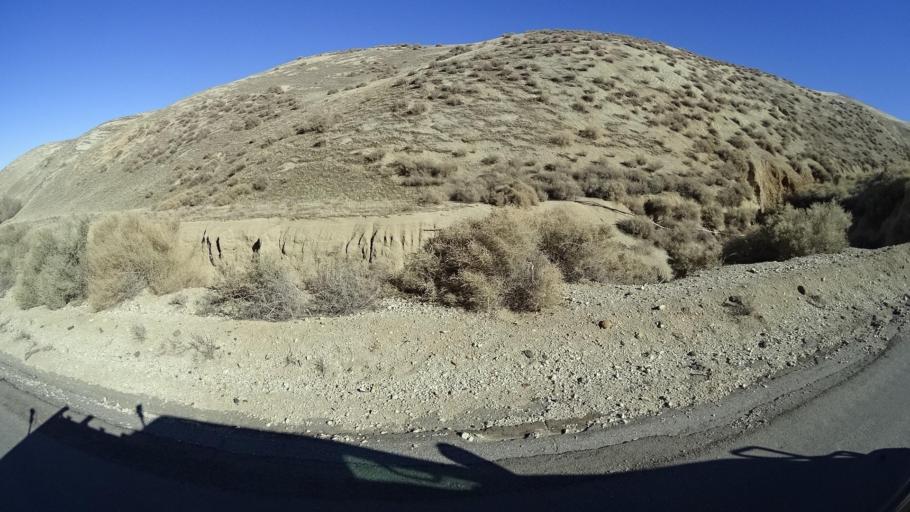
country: US
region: California
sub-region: Kern County
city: Maricopa
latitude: 34.9639
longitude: -119.4136
